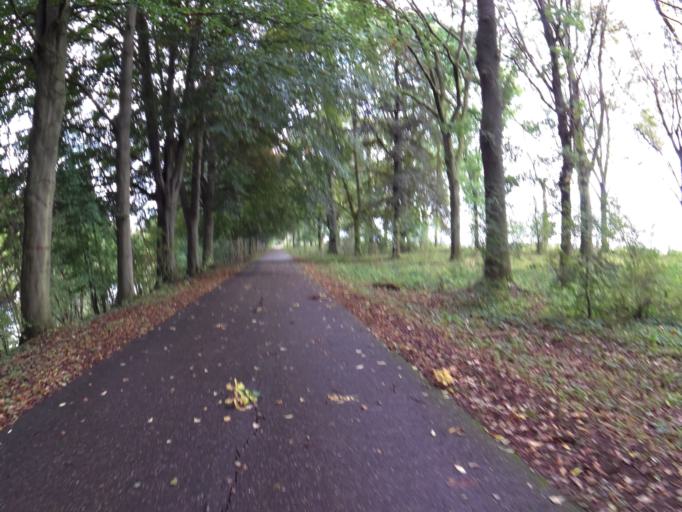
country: BE
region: Flanders
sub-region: Provincie Limburg
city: Lanaken
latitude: 50.8938
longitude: 5.6860
